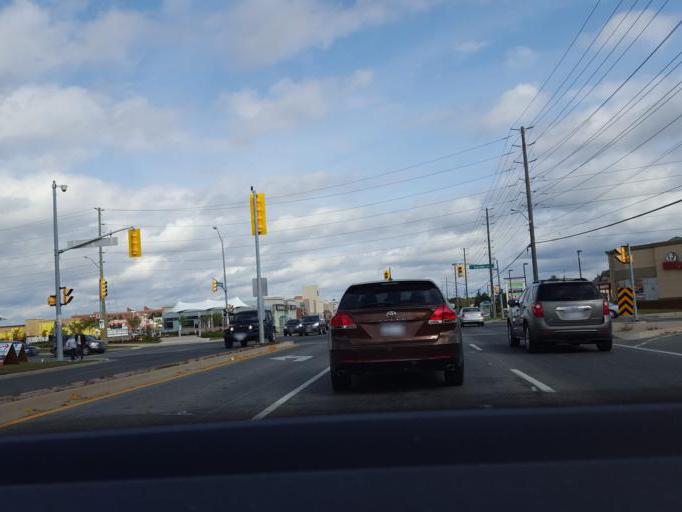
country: CA
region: Ontario
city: Oshawa
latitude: 43.9174
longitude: -78.9483
